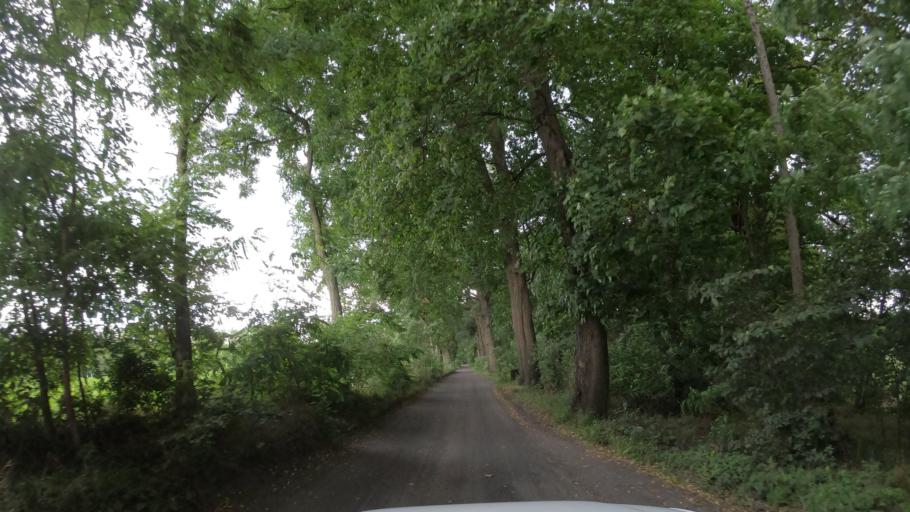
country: PL
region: West Pomeranian Voivodeship
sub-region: Powiat stargardzki
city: Dolice
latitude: 53.1940
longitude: 15.2829
